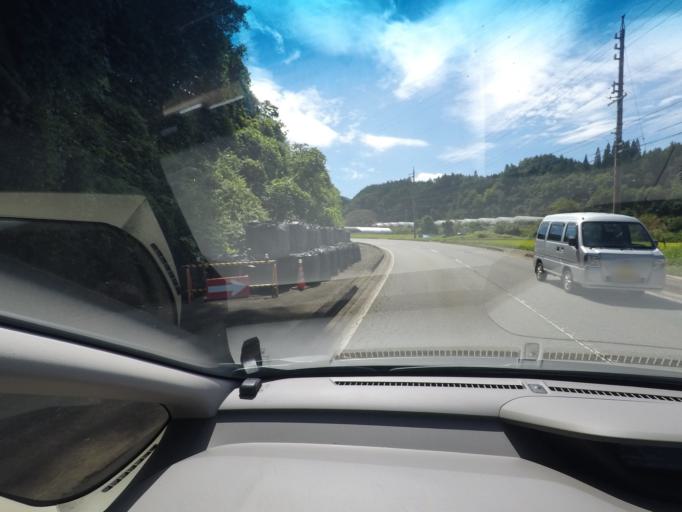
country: JP
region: Gifu
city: Takayama
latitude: 36.1407
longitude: 137.2850
